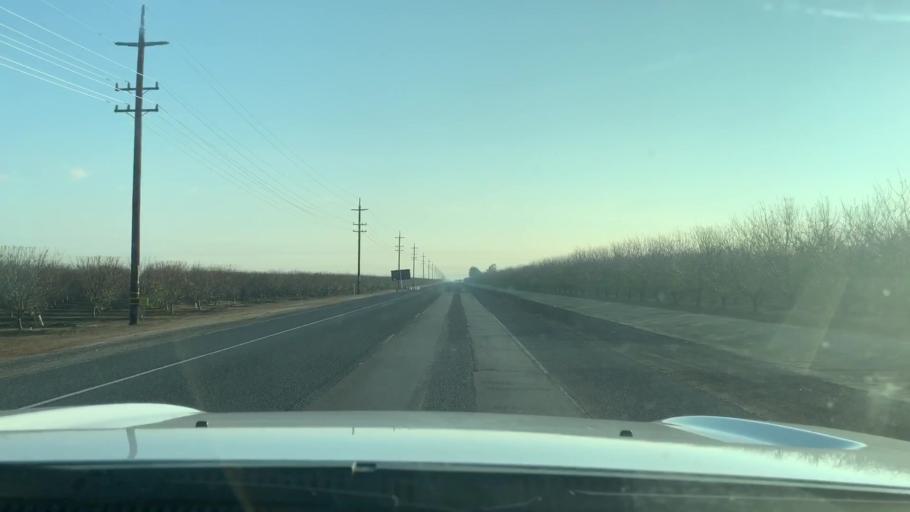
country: US
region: California
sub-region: Kern County
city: Wasco
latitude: 35.6014
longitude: -119.4329
